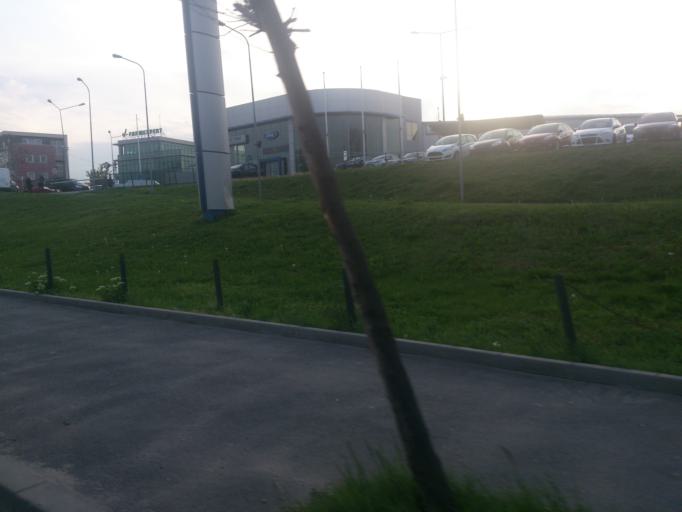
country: RO
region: Ilfov
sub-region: Comuna Chiajna
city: Rosu
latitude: 44.4452
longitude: 26.0376
